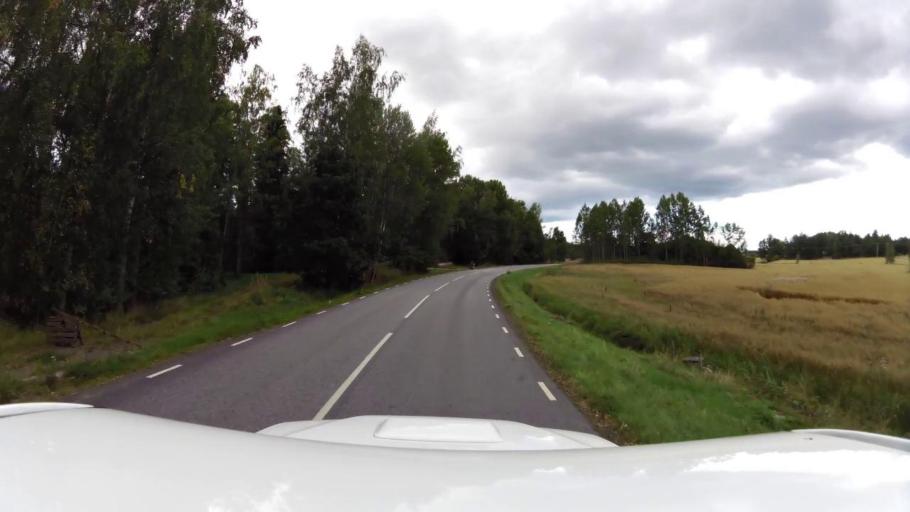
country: SE
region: OEstergoetland
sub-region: Linkopings Kommun
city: Linghem
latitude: 58.4116
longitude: 15.7626
